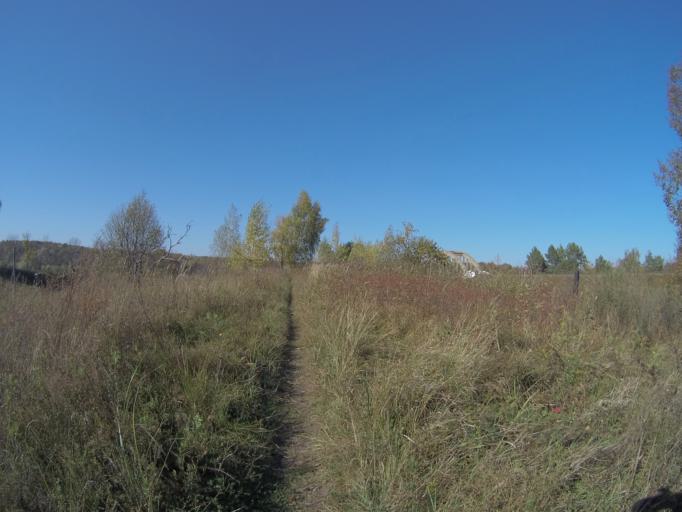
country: RU
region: Vladimir
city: Raduzhnyy
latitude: 56.0519
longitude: 40.3757
